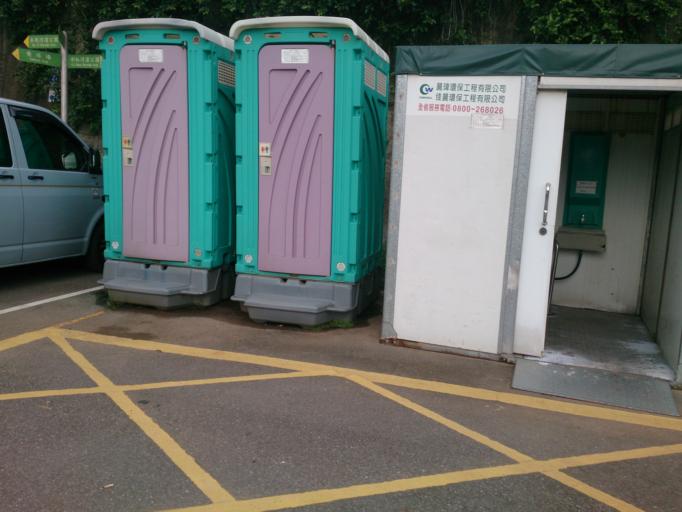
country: TW
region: Taipei
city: Taipei
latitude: 25.0644
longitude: 121.5721
